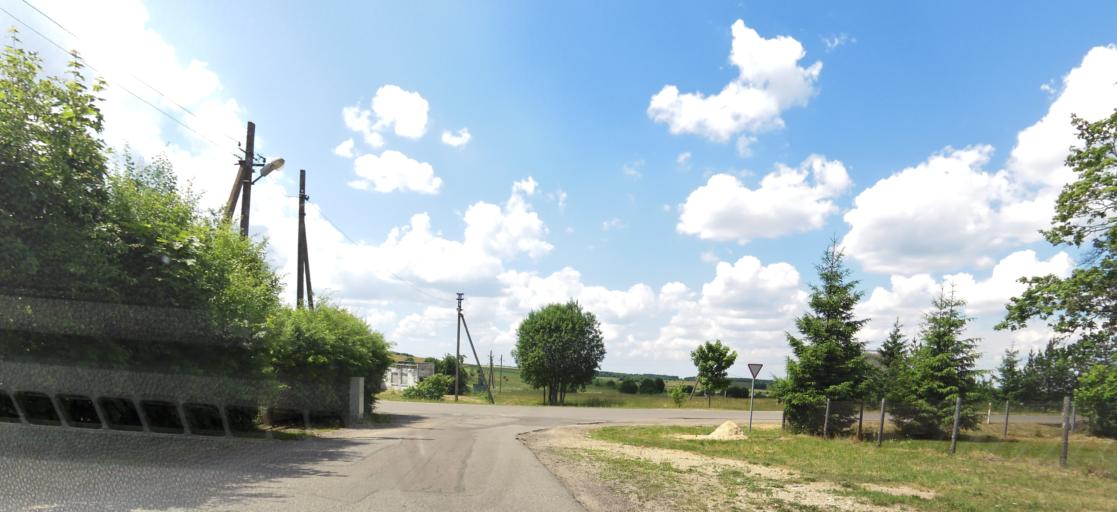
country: LT
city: Skaidiskes
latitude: 54.5378
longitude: 25.6460
